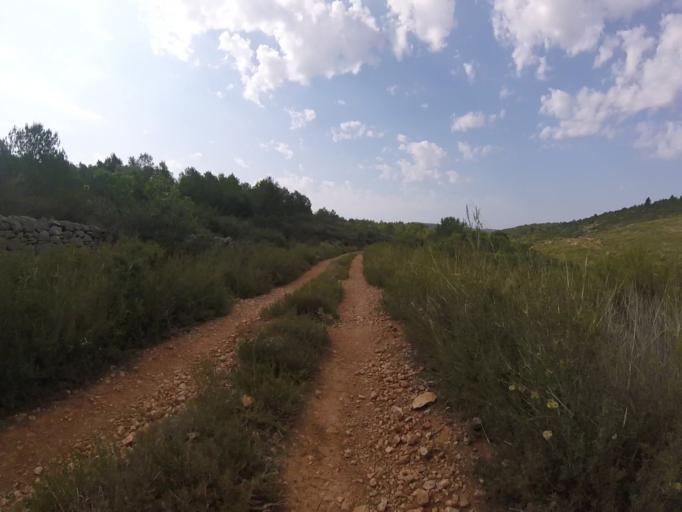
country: ES
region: Valencia
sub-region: Provincia de Castello
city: Alcala de Xivert
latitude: 40.3469
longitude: 0.1984
